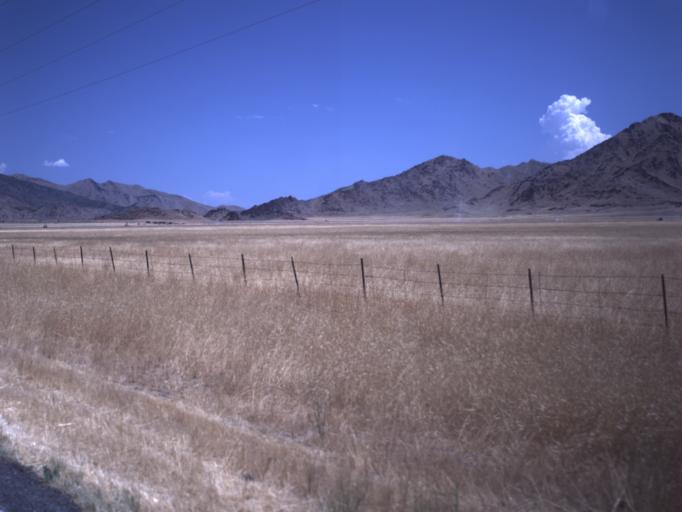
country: US
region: Utah
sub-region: Millard County
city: Delta
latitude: 39.4965
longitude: -112.2689
